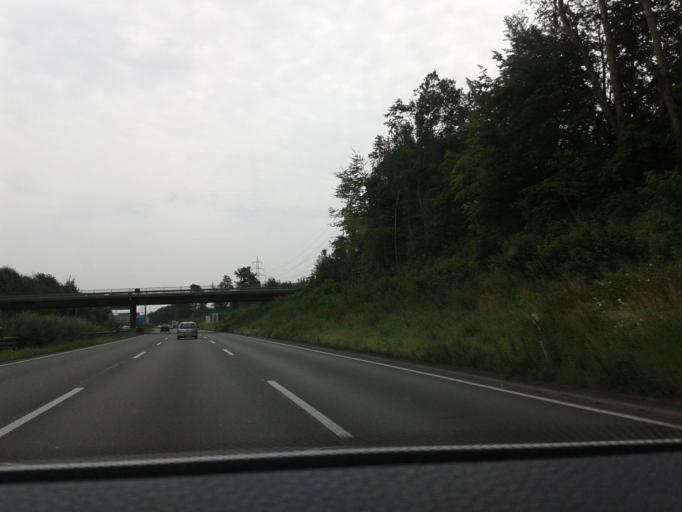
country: DE
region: North Rhine-Westphalia
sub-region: Regierungsbezirk Arnsberg
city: Unna
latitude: 51.5203
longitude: 7.6761
